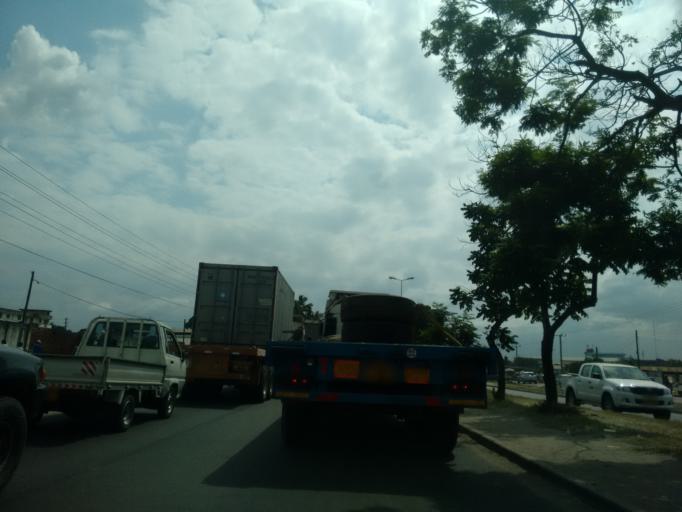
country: TZ
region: Dar es Salaam
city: Dar es Salaam
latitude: -6.8486
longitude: 39.2494
